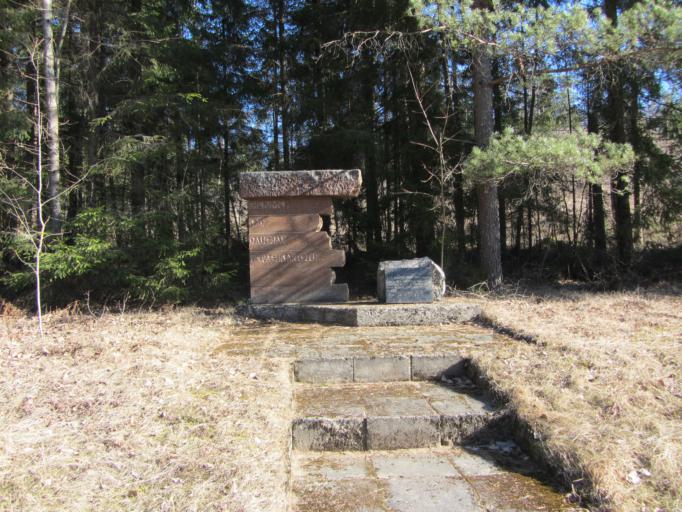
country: LT
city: Zarasai
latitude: 55.6867
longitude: 25.9896
